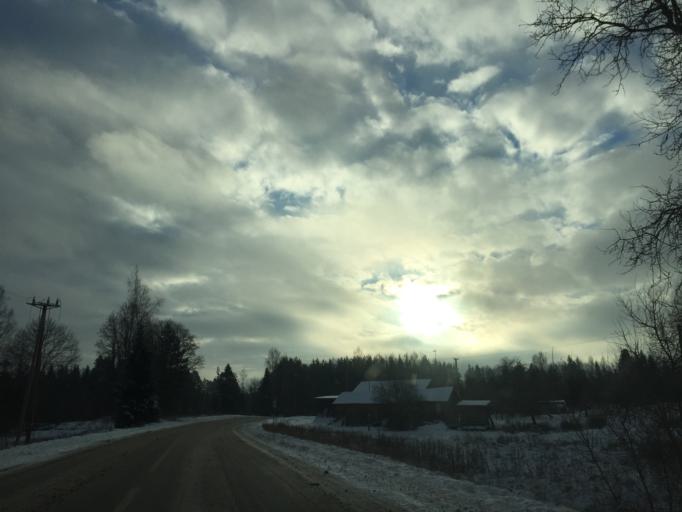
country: LV
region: Amatas Novads
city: Drabesi
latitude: 57.2277
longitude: 25.2796
